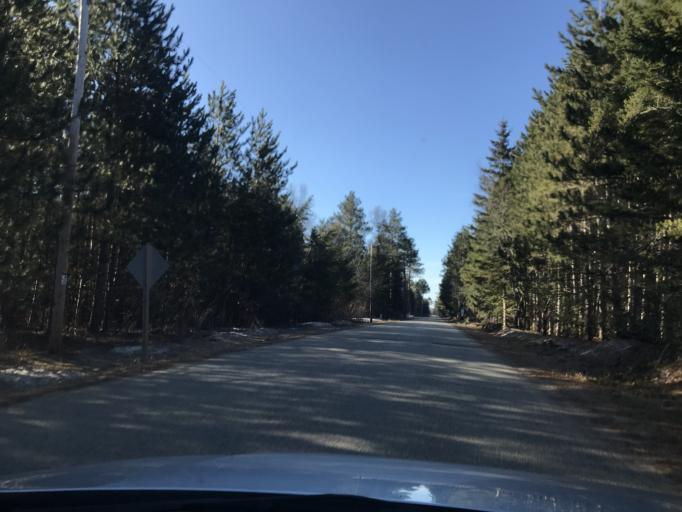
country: US
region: Michigan
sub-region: Dickinson County
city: Kingsford
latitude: 45.3988
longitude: -88.1609
